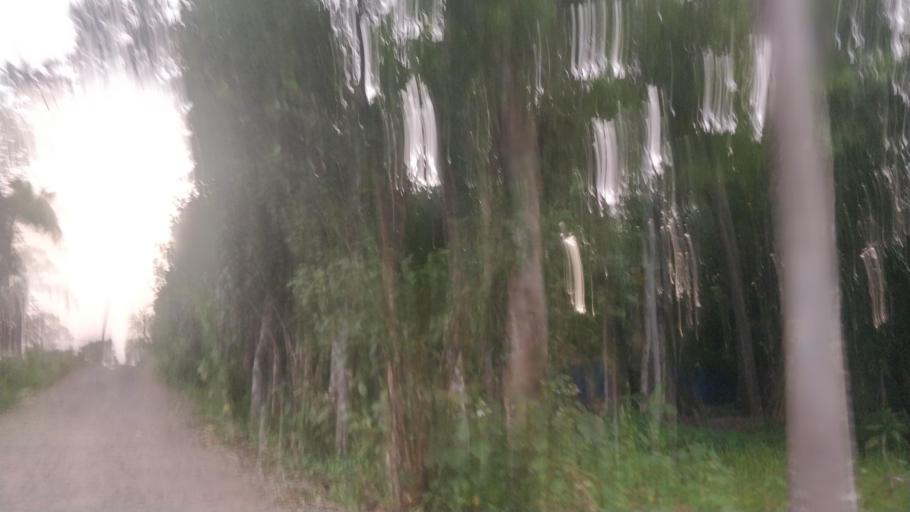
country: IN
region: Kerala
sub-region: Alappuzha
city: Shertallai
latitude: 9.6421
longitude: 76.3288
